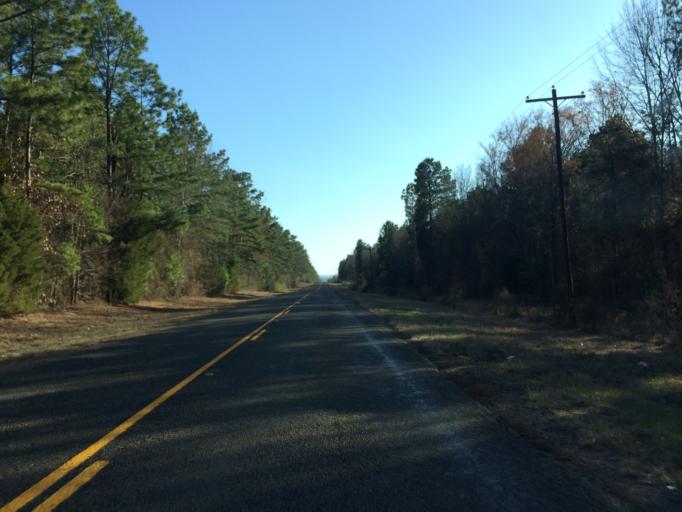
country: US
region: Texas
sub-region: Wood County
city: Hawkins
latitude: 32.6310
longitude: -95.3132
